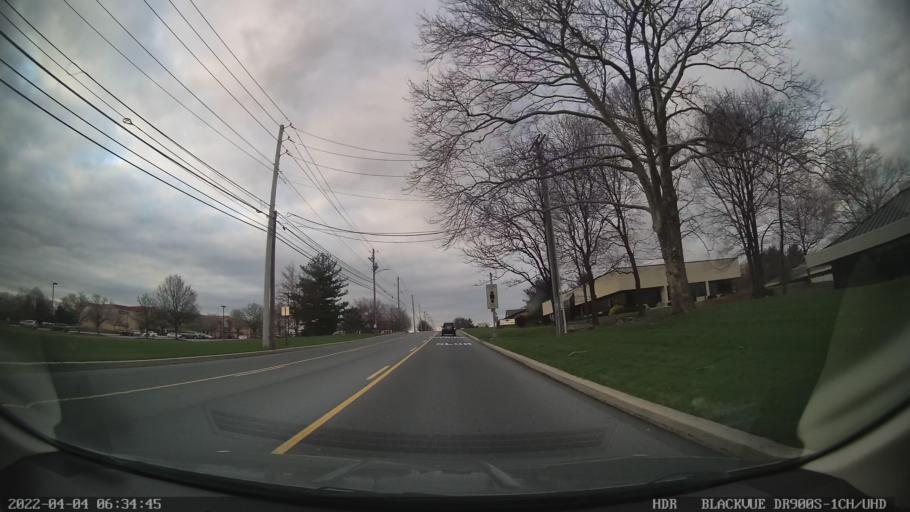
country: US
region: Pennsylvania
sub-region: Berks County
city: Spring Ridge
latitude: 40.3472
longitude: -75.9872
